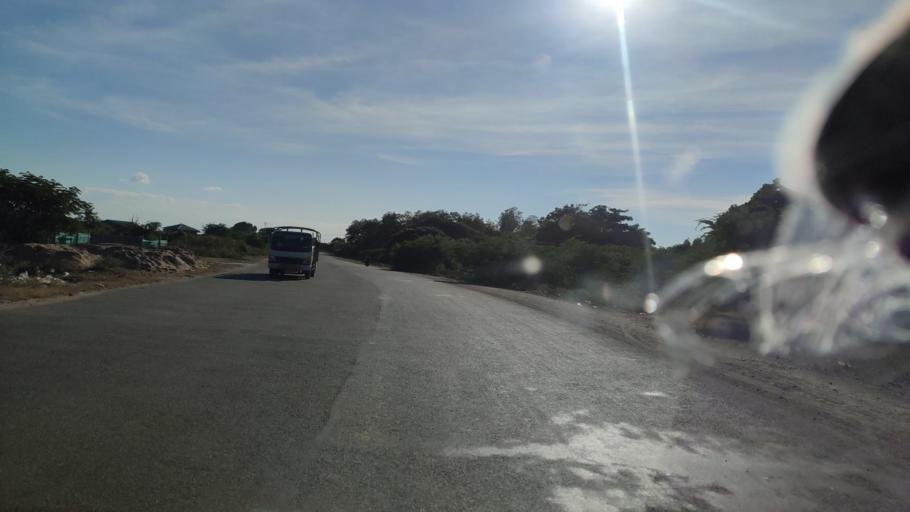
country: MM
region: Mandalay
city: Yamethin
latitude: 20.7478
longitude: 96.2334
